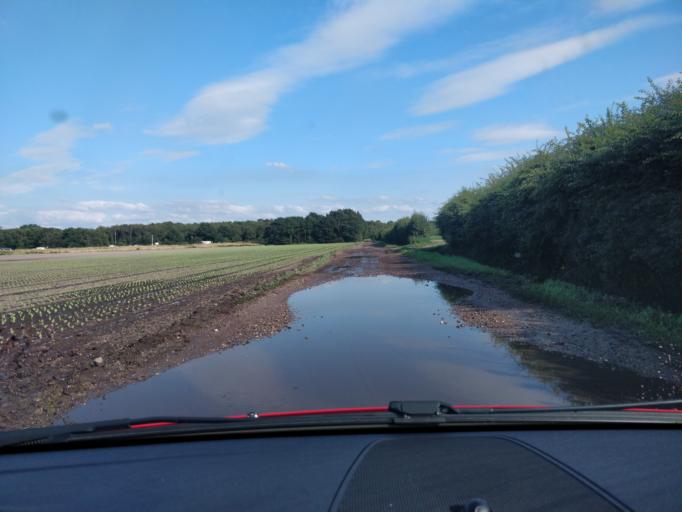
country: GB
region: England
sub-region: Lancashire
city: Banks
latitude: 53.6557
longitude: -2.9041
